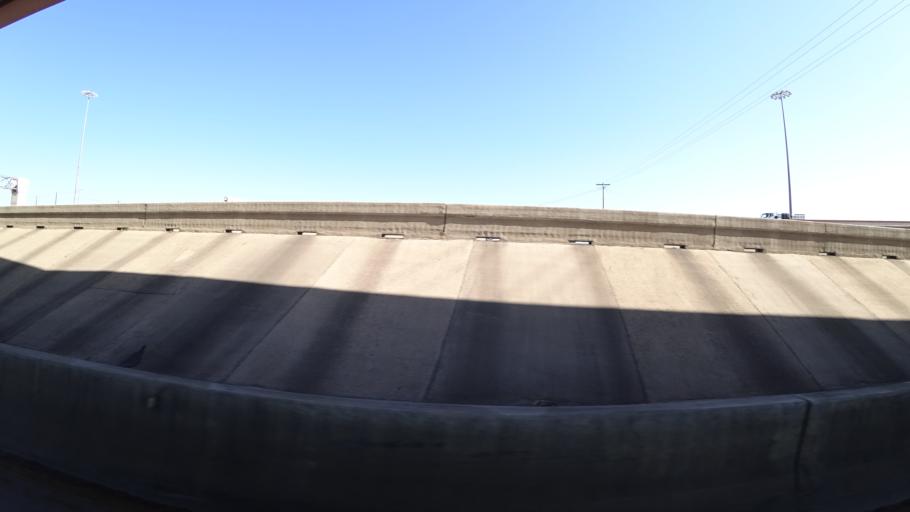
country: US
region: Texas
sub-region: Williamson County
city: Anderson Mill
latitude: 30.4748
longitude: -97.7999
